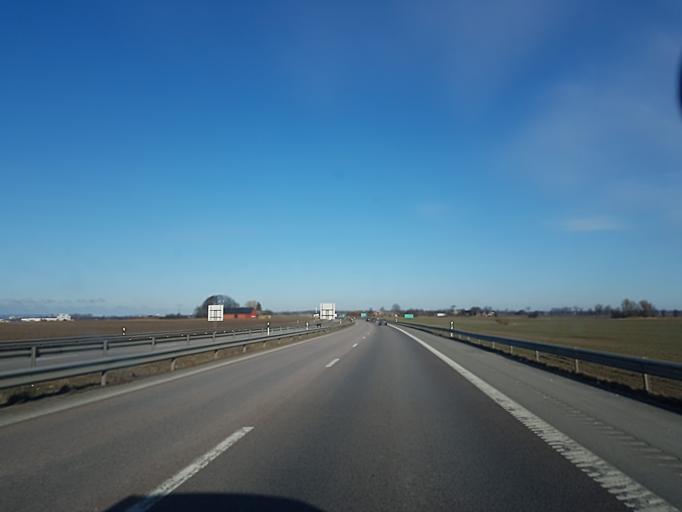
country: SE
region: Skane
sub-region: Helsingborg
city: Glumslov
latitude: 55.9575
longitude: 12.8026
